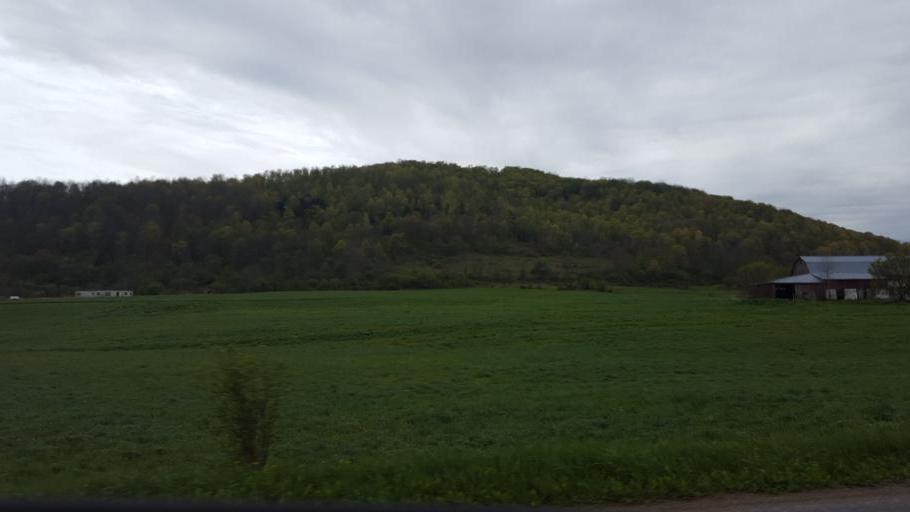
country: US
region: Pennsylvania
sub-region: Tioga County
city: Westfield
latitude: 41.9204
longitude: -77.6238
